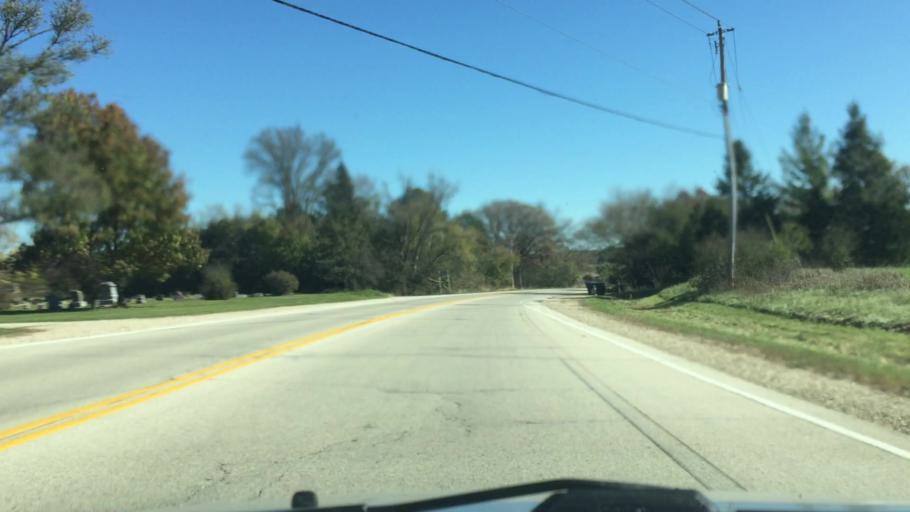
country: US
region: Wisconsin
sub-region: Waukesha County
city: North Prairie
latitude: 42.9302
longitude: -88.4241
